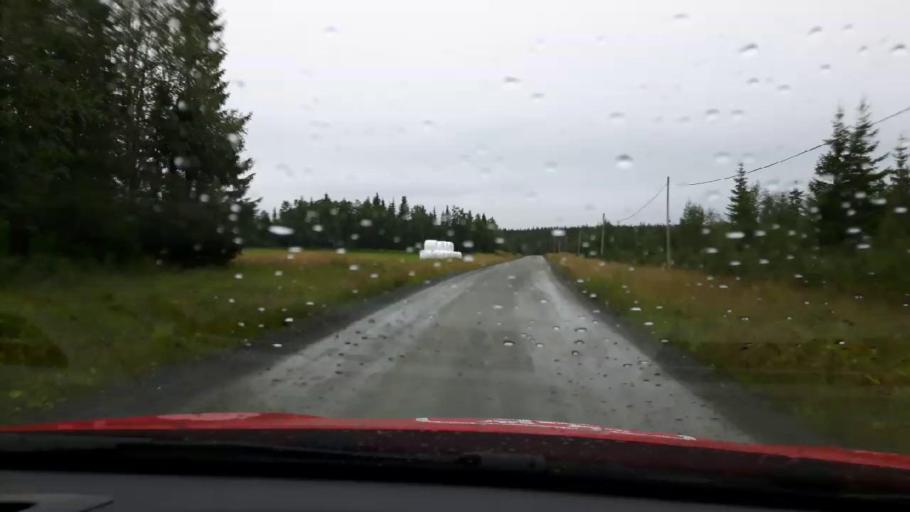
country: SE
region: Jaemtland
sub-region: Are Kommun
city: Are
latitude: 63.4409
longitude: 12.8077
